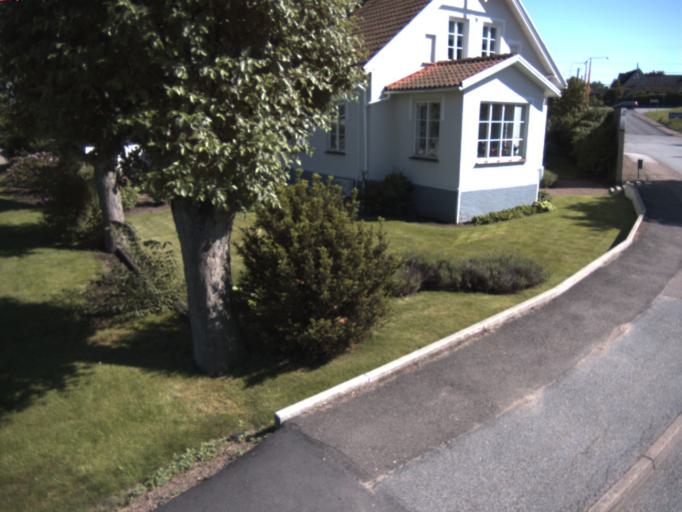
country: SE
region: Skane
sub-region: Helsingborg
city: Gantofta
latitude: 55.9917
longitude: 12.8041
